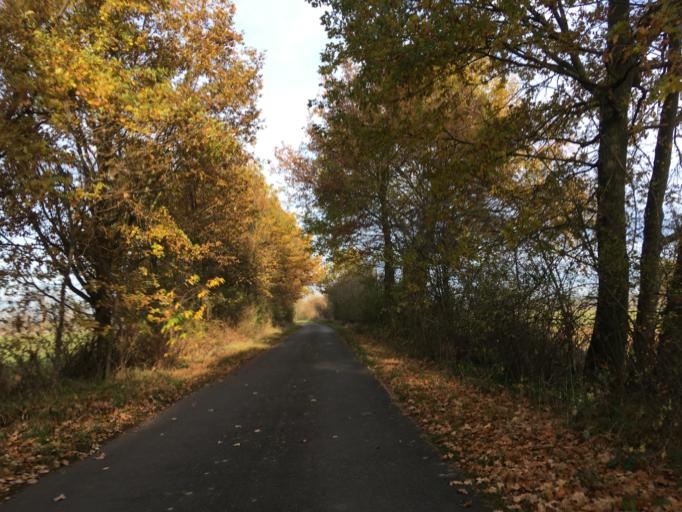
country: DE
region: Brandenburg
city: Luebben
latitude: 51.9753
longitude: 13.8772
